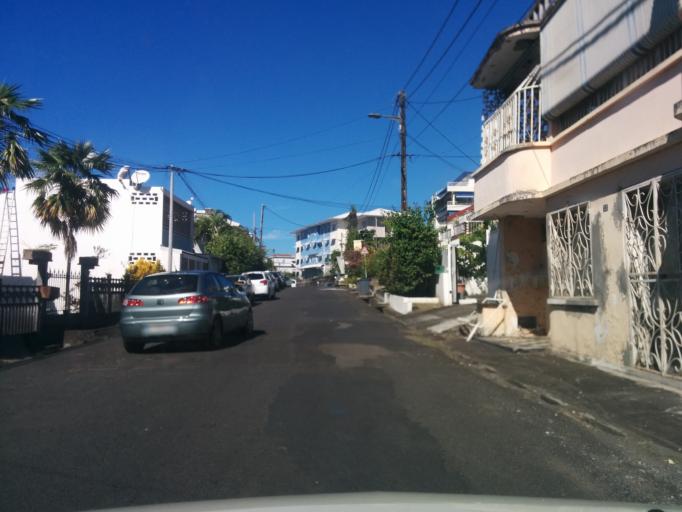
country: MQ
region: Martinique
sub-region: Martinique
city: Fort-de-France
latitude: 14.6045
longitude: -61.0791
